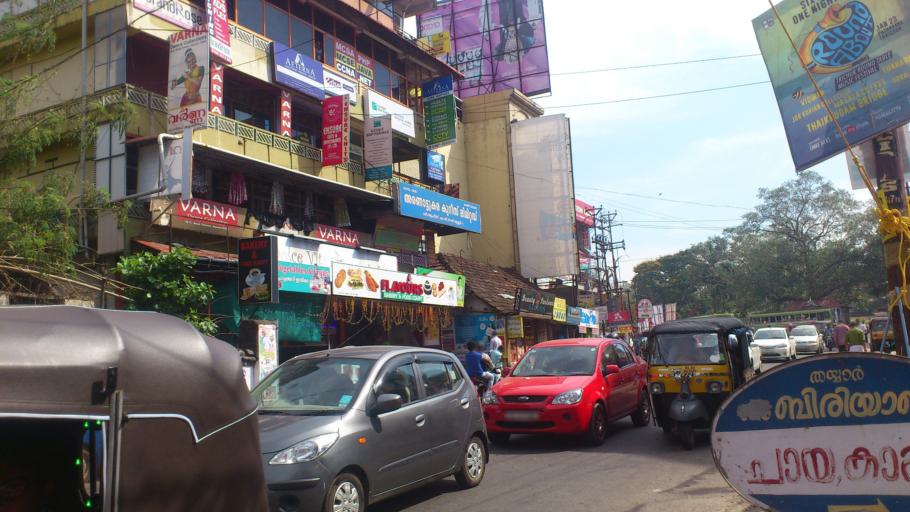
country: IN
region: Kerala
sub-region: Thrissur District
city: Trichur
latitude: 10.5239
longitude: 76.2108
